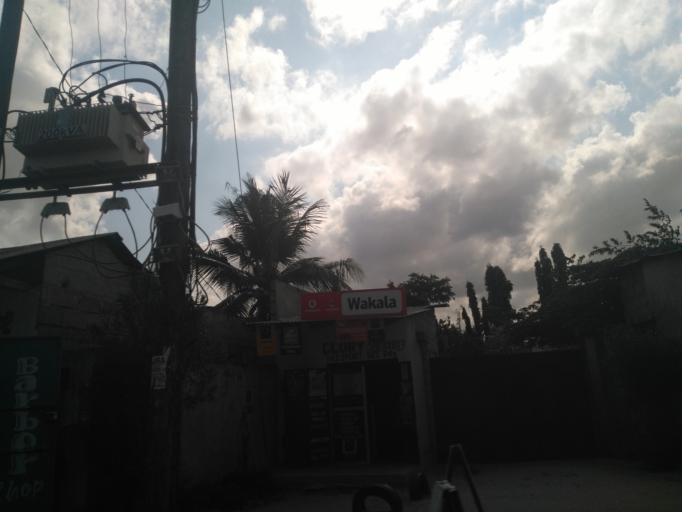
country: TZ
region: Dar es Salaam
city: Dar es Salaam
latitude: -6.8991
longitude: 39.2833
